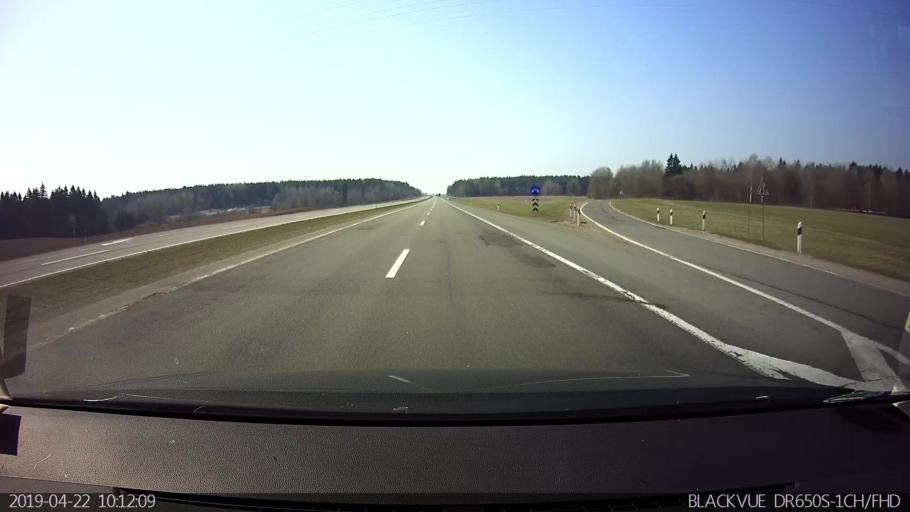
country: BY
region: Vitebsk
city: Horad Orsha
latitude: 54.5957
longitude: 30.3493
